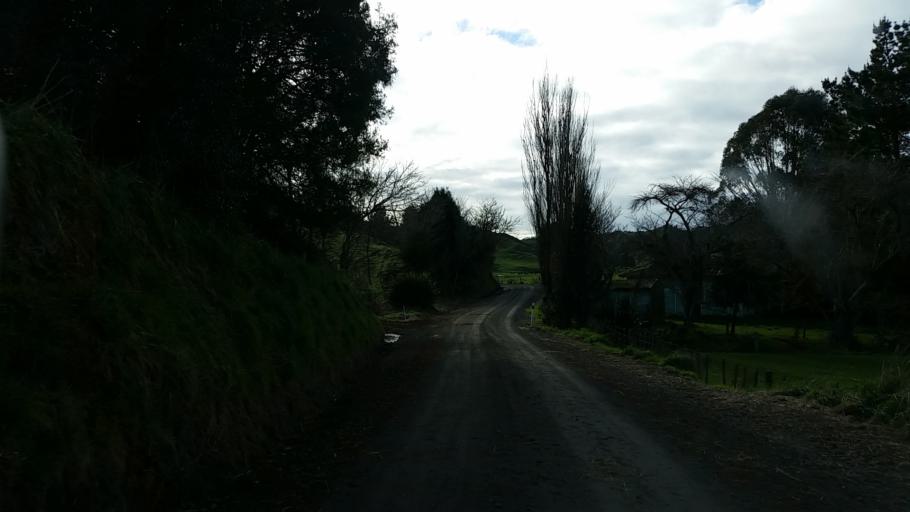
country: NZ
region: Taranaki
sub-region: South Taranaki District
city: Eltham
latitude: -39.2534
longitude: 174.5318
